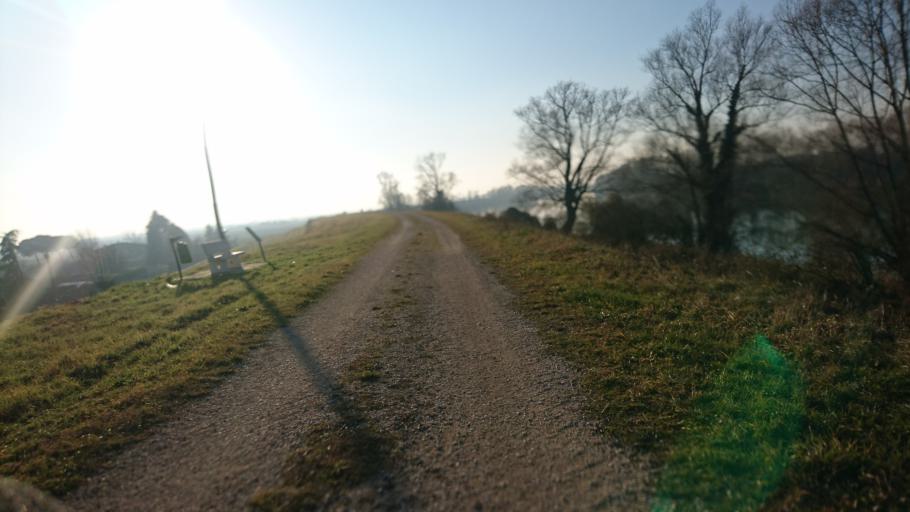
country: IT
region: Veneto
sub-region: Provincia di Rovigo
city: San Martino di Venezze
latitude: 45.1310
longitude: 11.8577
